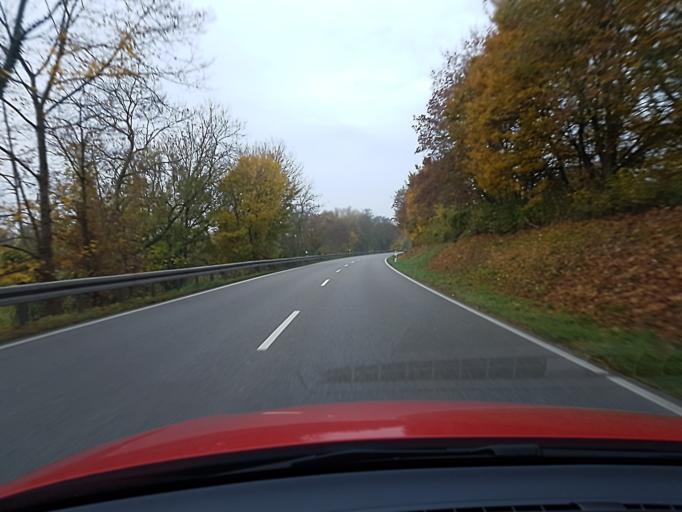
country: DE
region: Baden-Wuerttemberg
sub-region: Regierungsbezirk Stuttgart
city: Walheim
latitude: 49.0097
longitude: 9.1561
